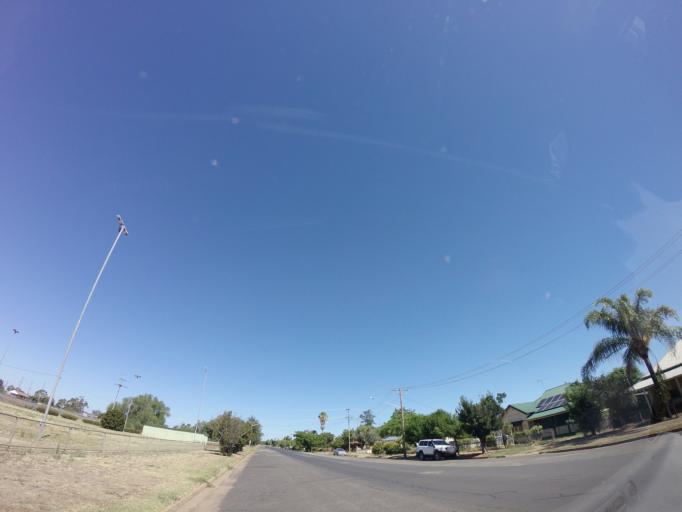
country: AU
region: New South Wales
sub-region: Bogan
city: Nyngan
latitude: -31.5642
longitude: 147.1986
